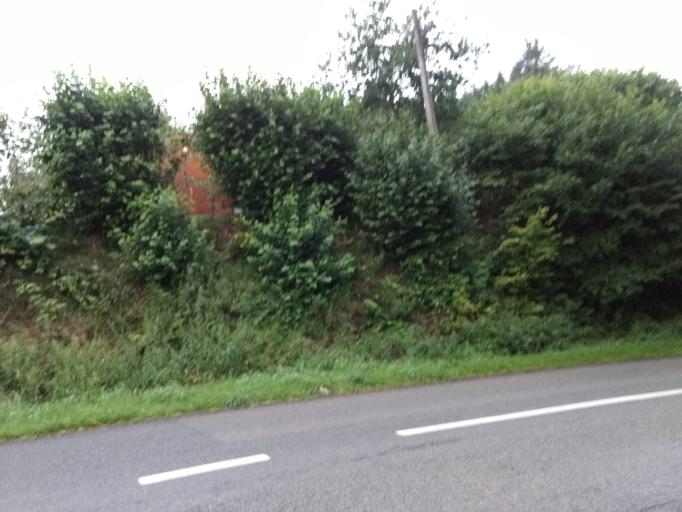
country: BE
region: Wallonia
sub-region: Province du Luxembourg
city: Houffalize
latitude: 50.1491
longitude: 5.7196
